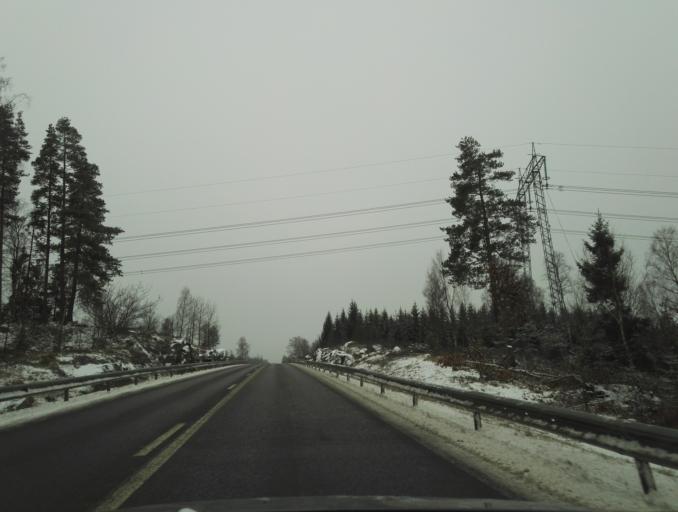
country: SE
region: Kronoberg
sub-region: Vaxjo Kommun
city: Gemla
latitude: 56.8249
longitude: 14.6909
